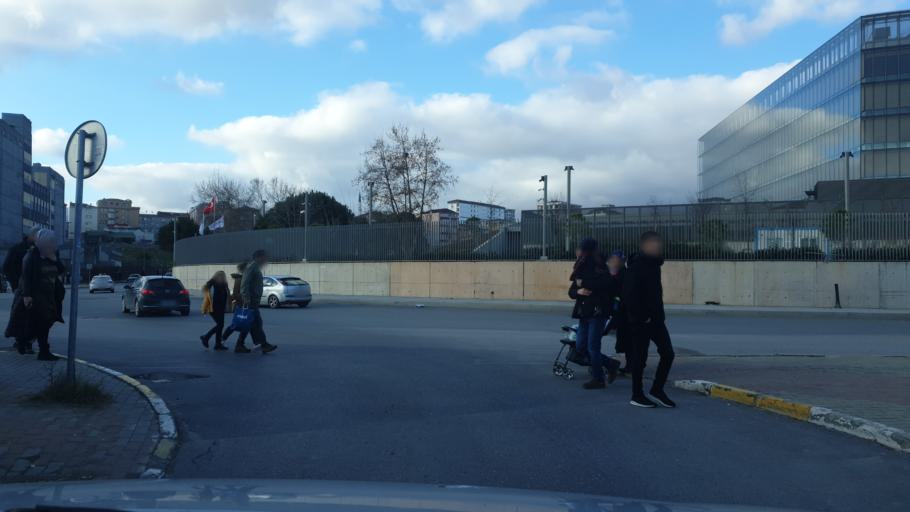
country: TR
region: Istanbul
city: Pendik
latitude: 40.8670
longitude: 29.2767
